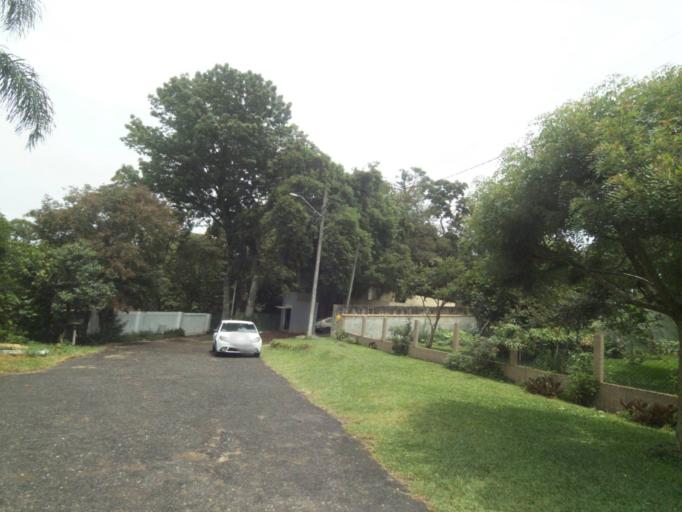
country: BR
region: Parana
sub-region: Curitiba
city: Curitiba
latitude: -25.4160
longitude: -49.2919
